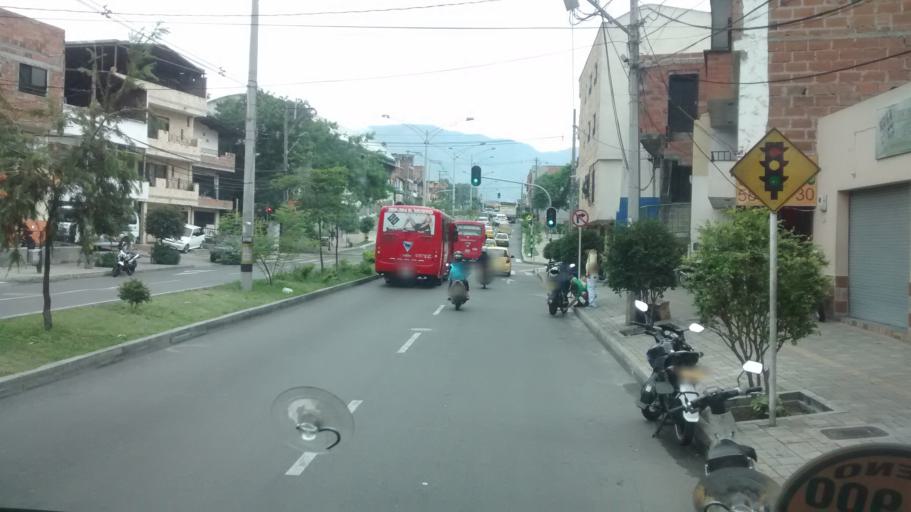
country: CO
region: Antioquia
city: Bello
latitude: 6.2985
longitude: -75.5668
